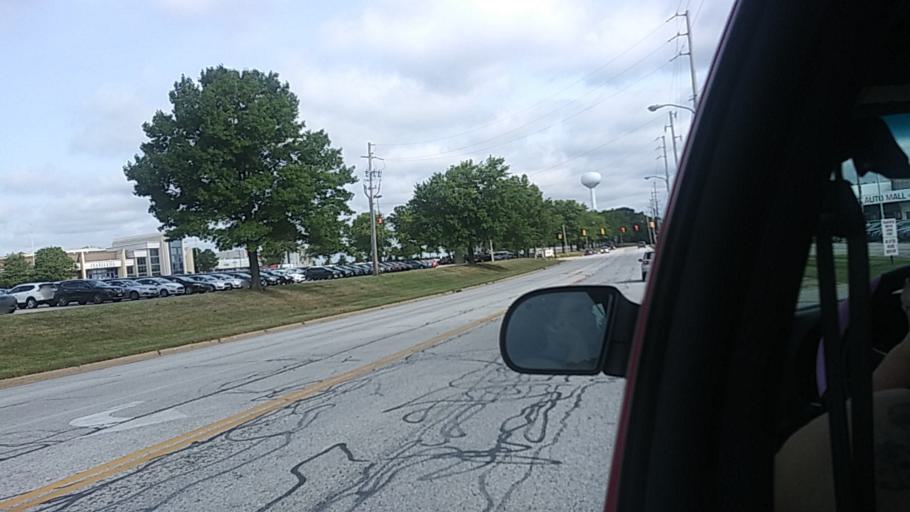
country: US
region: Ohio
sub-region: Summit County
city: Tallmadge
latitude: 41.1129
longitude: -81.4660
